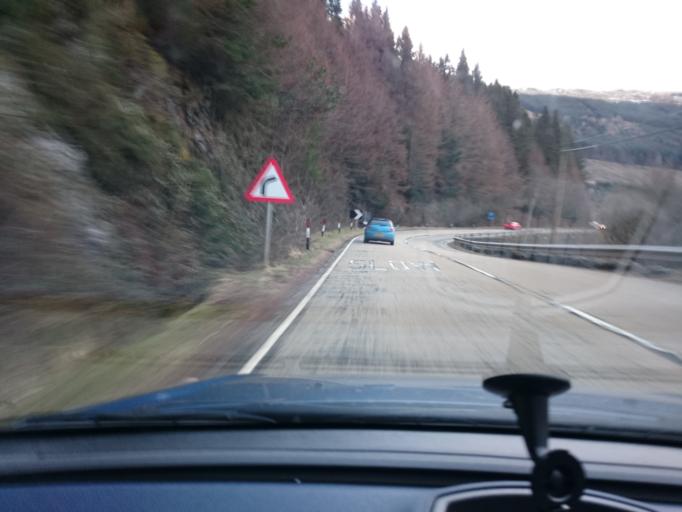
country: GB
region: Scotland
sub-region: Stirling
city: Callander
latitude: 56.2962
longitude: -4.2999
